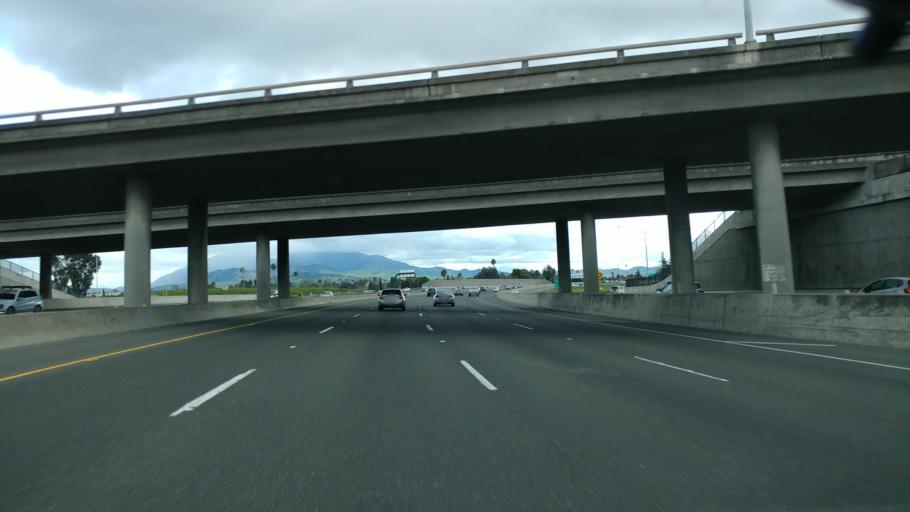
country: US
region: California
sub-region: Contra Costa County
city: Pacheco
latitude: 37.9949
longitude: -122.0704
